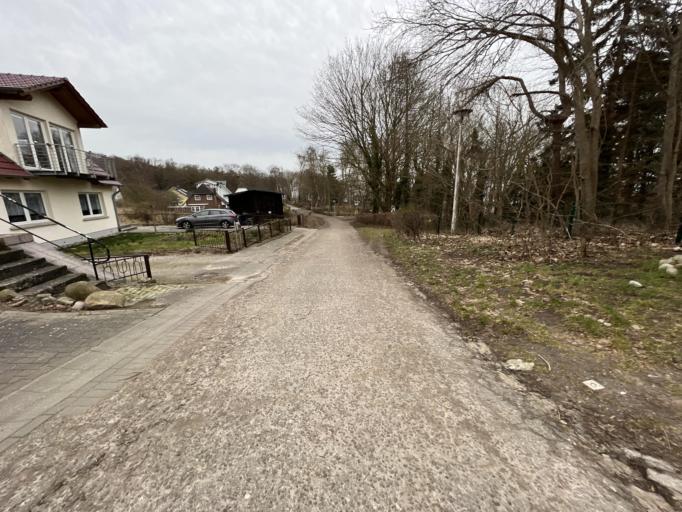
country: DE
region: Mecklenburg-Vorpommern
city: Ostseebad Gohren
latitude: 54.3396
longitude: 13.7505
